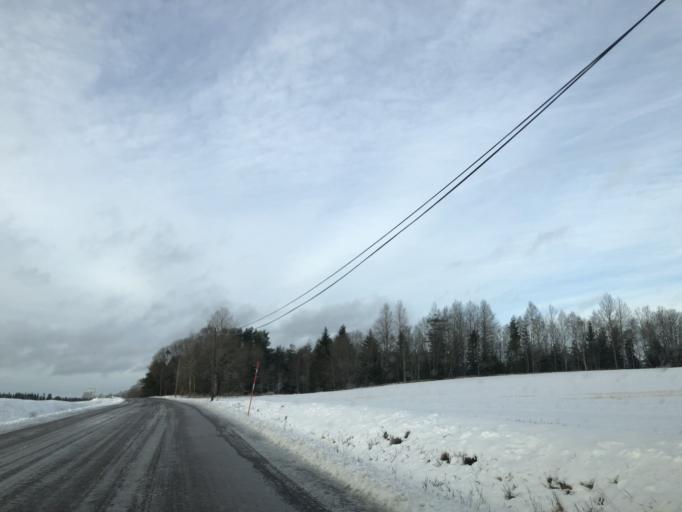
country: SE
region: Vaestra Goetaland
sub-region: Ulricehamns Kommun
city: Ulricehamn
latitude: 57.8124
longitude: 13.5362
